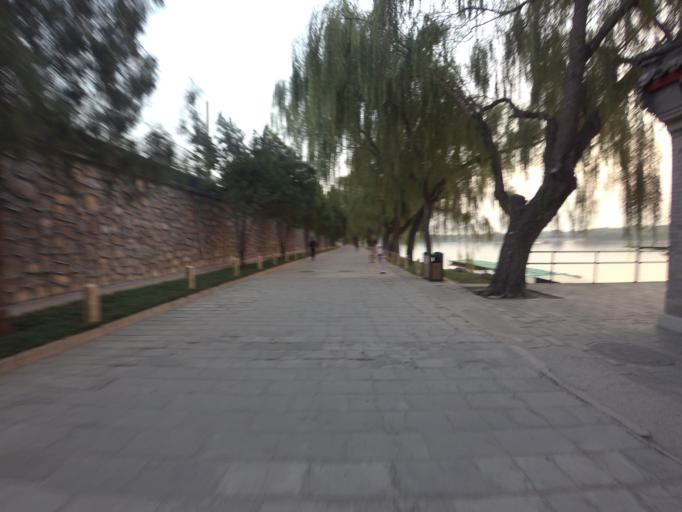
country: CN
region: Beijing
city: Haidian
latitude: 39.9883
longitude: 116.2725
